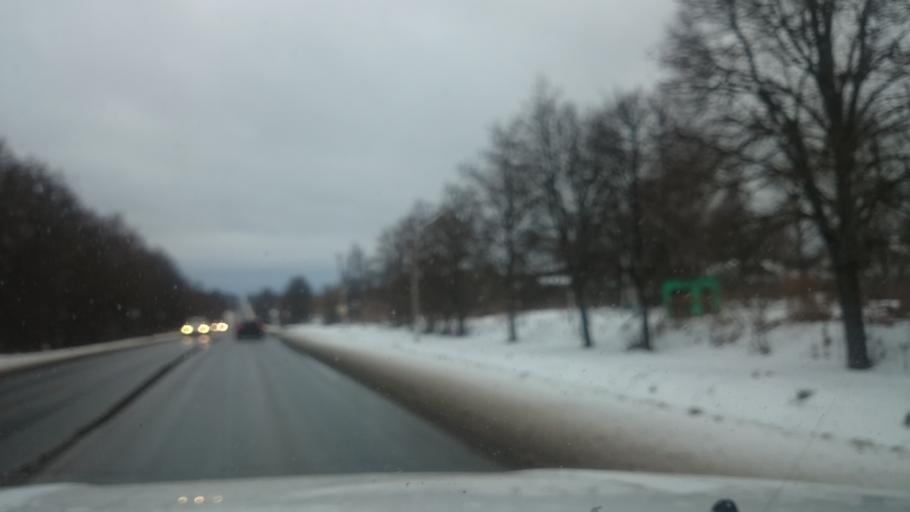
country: RU
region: Tula
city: Kosaya Gora
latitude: 54.1102
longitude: 37.5551
